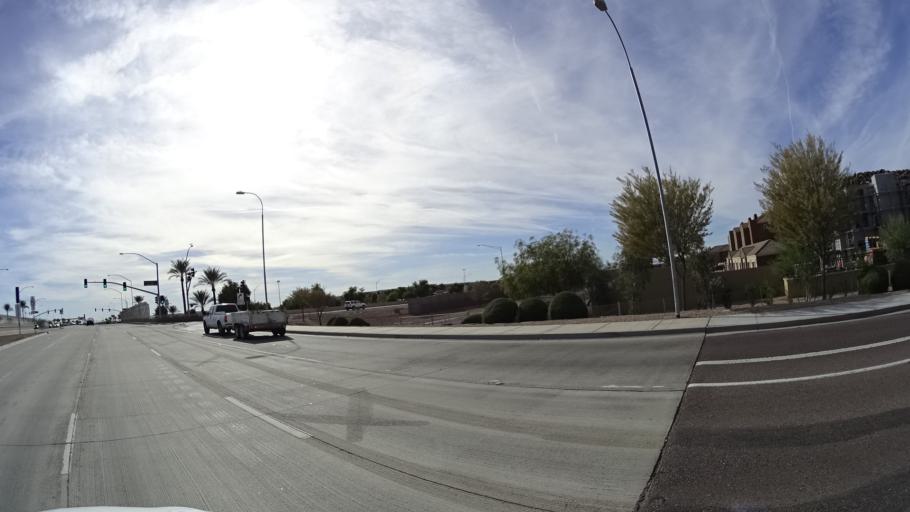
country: US
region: Arizona
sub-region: Maricopa County
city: Chandler
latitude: 33.2839
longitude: -111.8070
